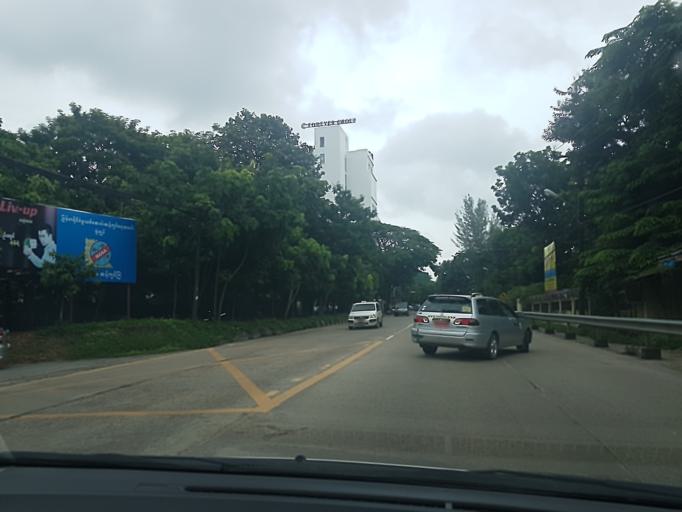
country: MM
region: Yangon
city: Yangon
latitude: 16.8137
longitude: 96.1323
